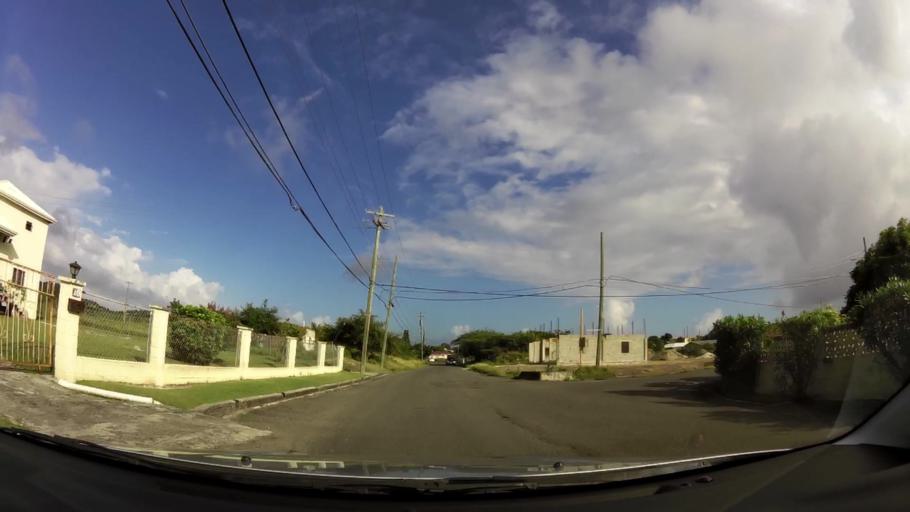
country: AG
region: Saint John
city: Saint John's
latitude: 17.1290
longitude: -61.8346
